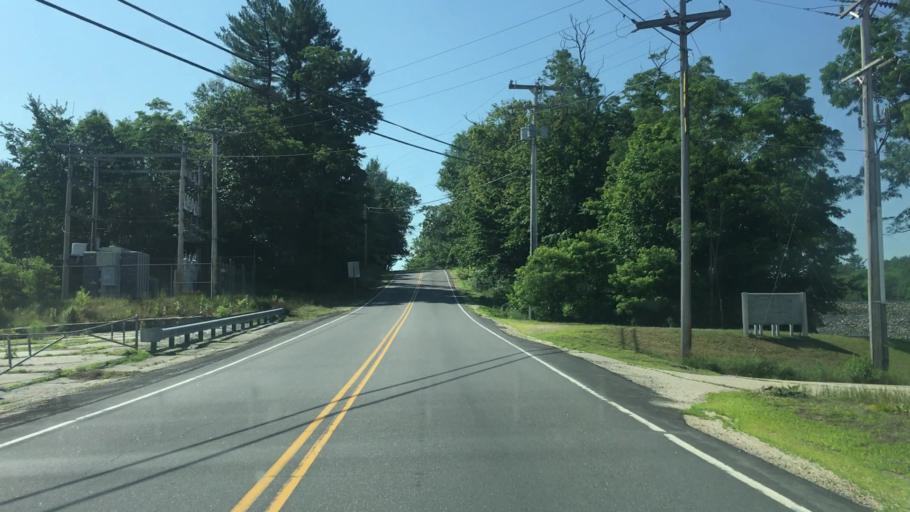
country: US
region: New Hampshire
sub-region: Merrimack County
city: Contoocook
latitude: 43.1916
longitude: -71.7479
